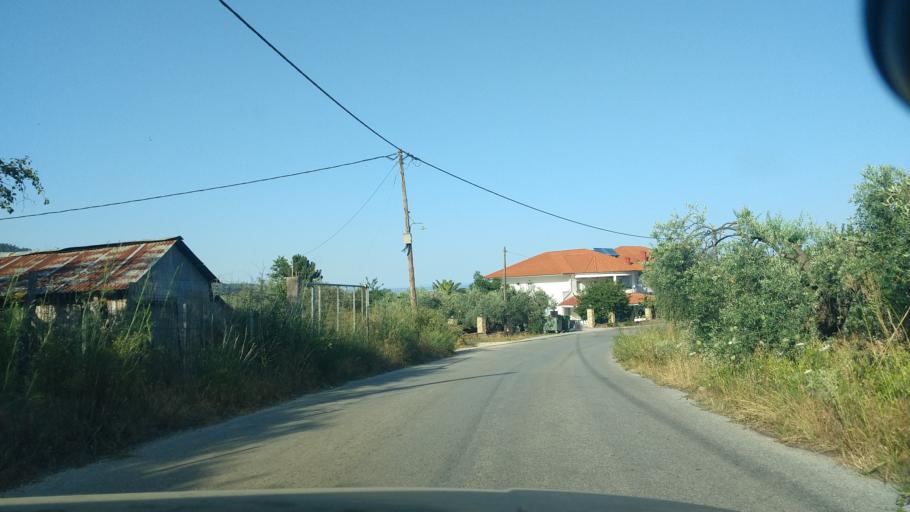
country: GR
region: East Macedonia and Thrace
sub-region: Nomos Kavalas
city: Potamia
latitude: 40.7165
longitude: 24.7433
